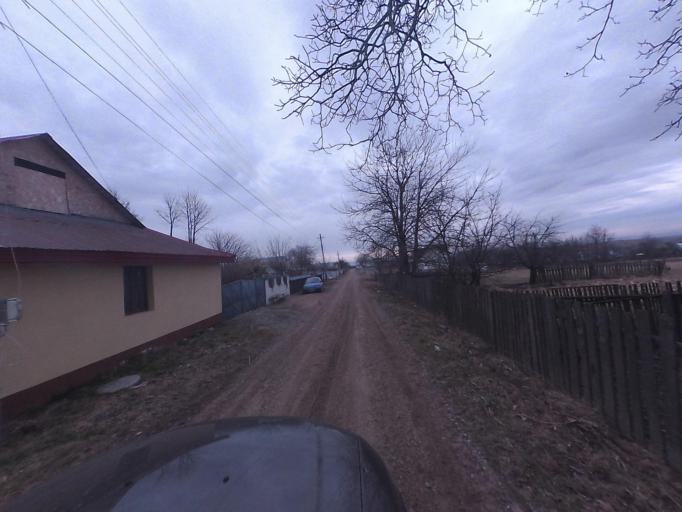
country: RO
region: Neamt
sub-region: Oras Targu Neamt
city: Humulesti
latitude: 47.1912
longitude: 26.3361
